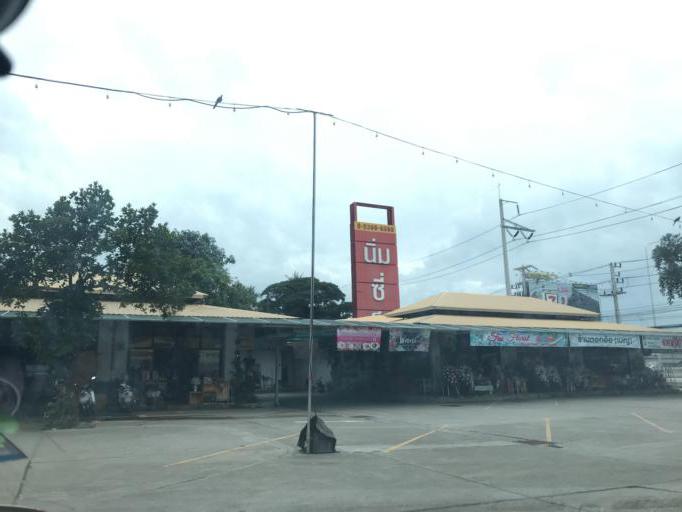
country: TH
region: Chiang Mai
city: Chiang Mai
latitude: 18.8091
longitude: 99.0088
